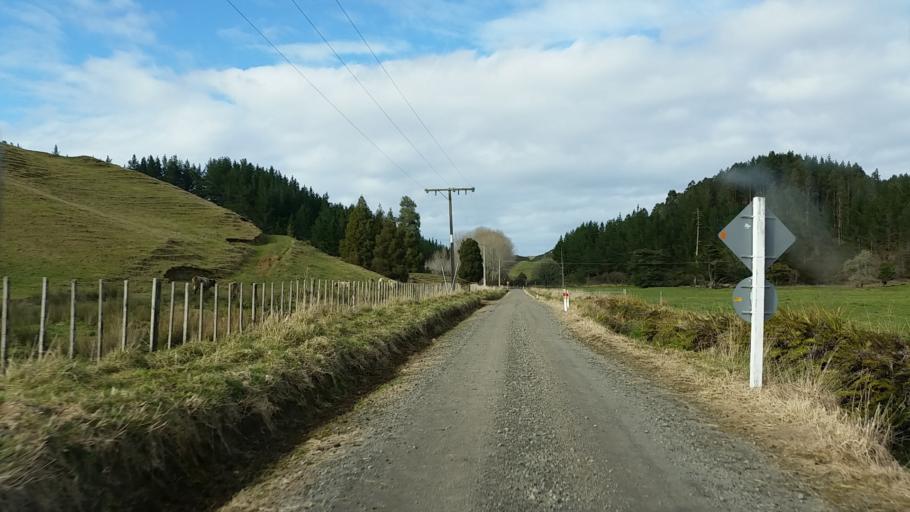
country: NZ
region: Taranaki
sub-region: South Taranaki District
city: Eltham
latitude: -39.2308
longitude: 174.5662
